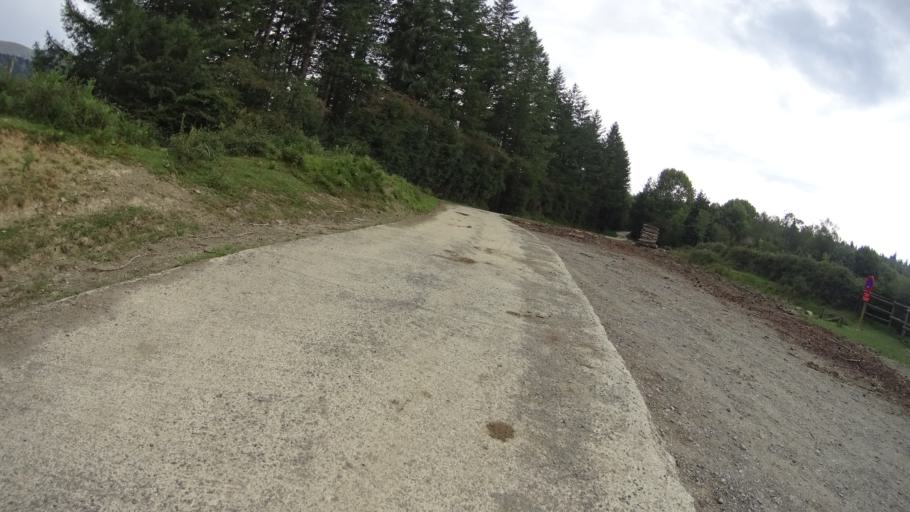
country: ES
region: Basque Country
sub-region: Bizkaia
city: Zeanuri
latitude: 43.0515
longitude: -2.7300
